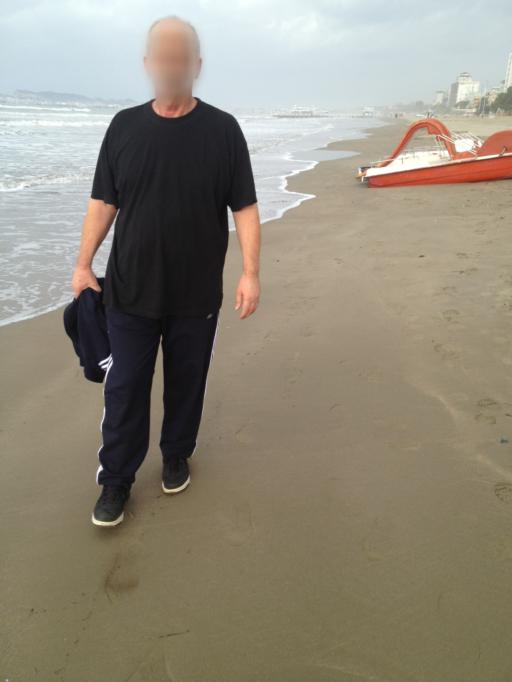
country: AL
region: Tirane
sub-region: Rrethi i Kavajes
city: Golem
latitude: 41.2772
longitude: 19.5142
